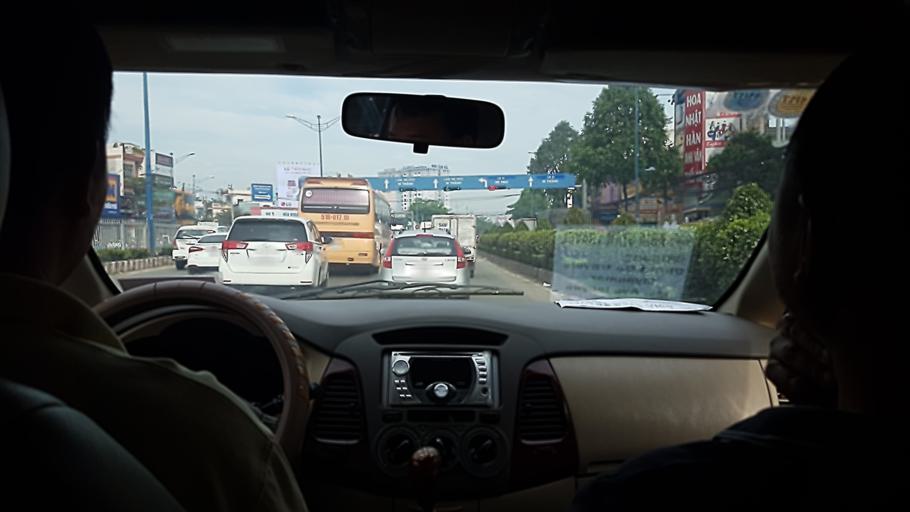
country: VN
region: Ho Chi Minh City
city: Ho Chi Minh City
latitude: 10.8266
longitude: 106.6260
